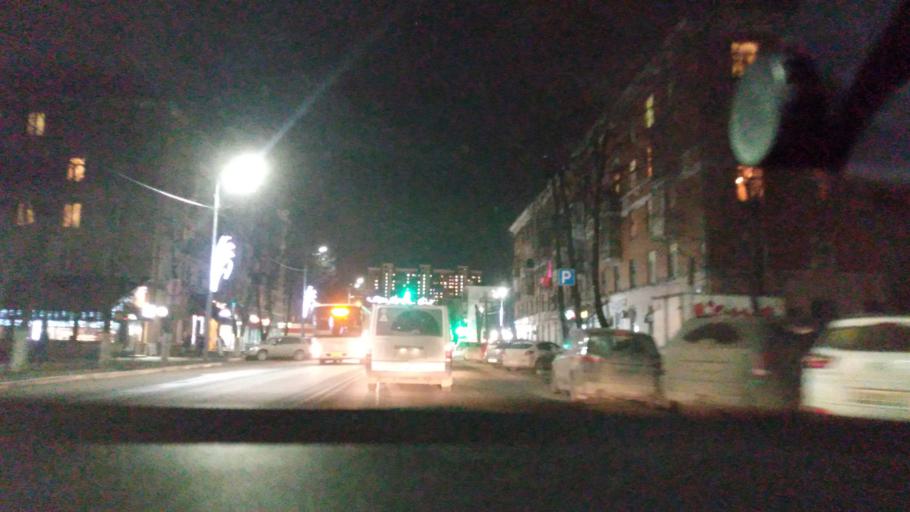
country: RU
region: Moskovskaya
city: Balashikha
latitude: 55.7983
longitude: 37.9345
